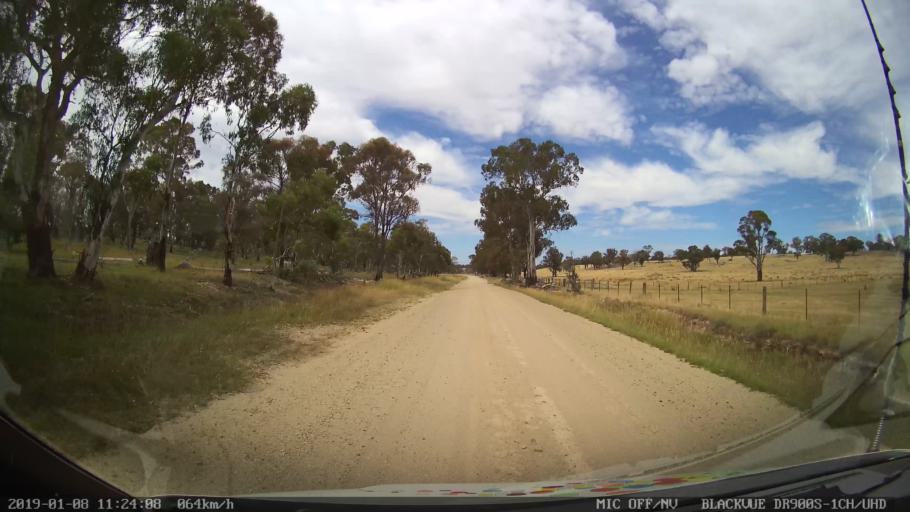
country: AU
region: New South Wales
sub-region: Guyra
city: Guyra
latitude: -30.2618
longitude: 151.5583
